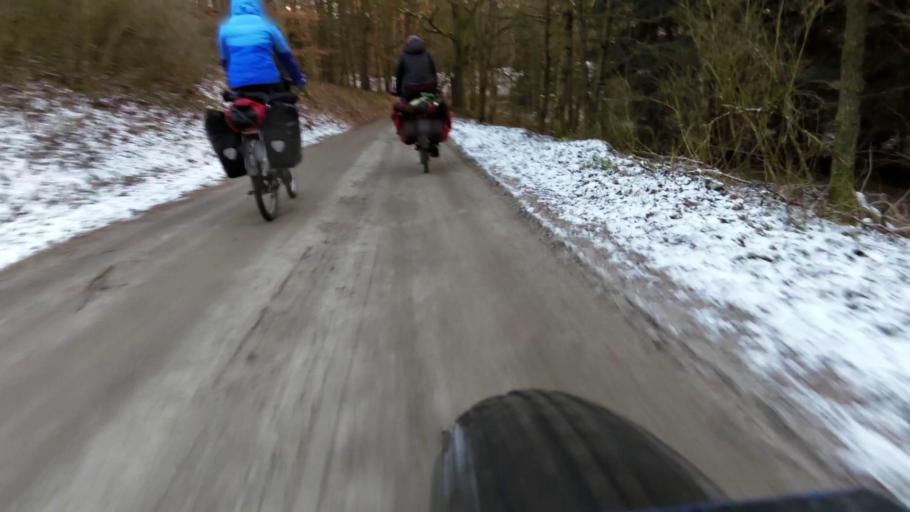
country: PL
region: West Pomeranian Voivodeship
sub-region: Powiat walecki
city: Walcz
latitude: 53.2503
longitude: 16.3728
